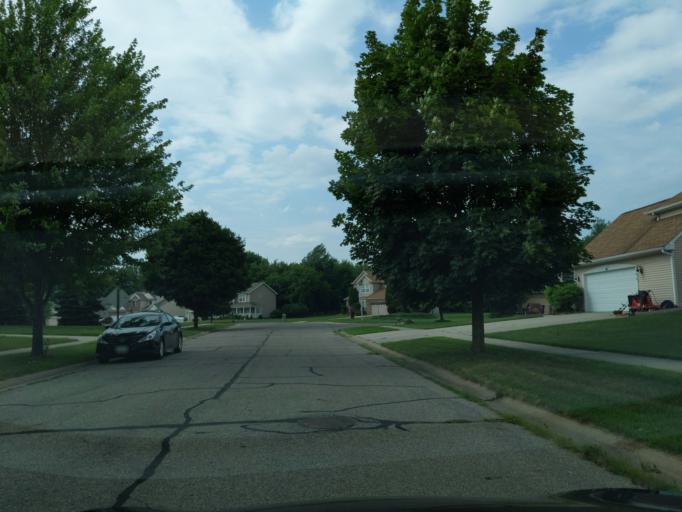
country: US
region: Michigan
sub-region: Ingham County
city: Okemos
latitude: 42.7361
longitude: -84.4296
